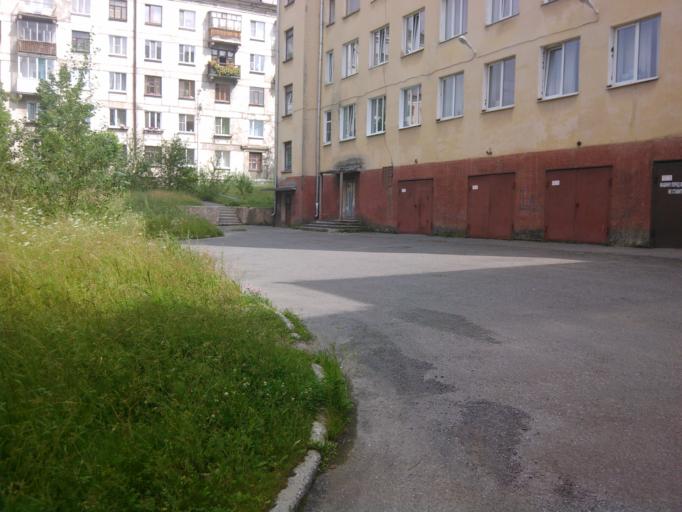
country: RU
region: Sverdlovsk
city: Krasnotur'insk
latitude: 59.7650
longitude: 60.1931
